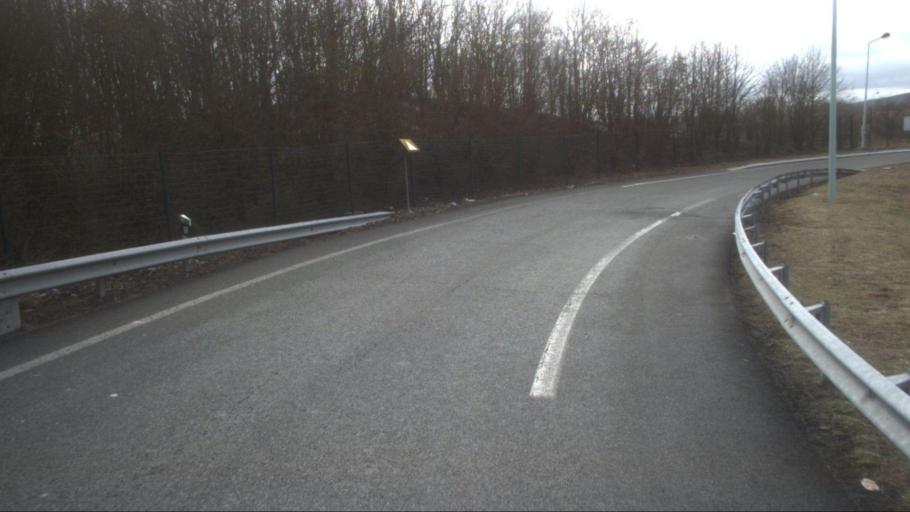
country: FR
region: Ile-de-France
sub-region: Departement des Yvelines
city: Houdan
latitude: 48.7916
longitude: 1.6338
